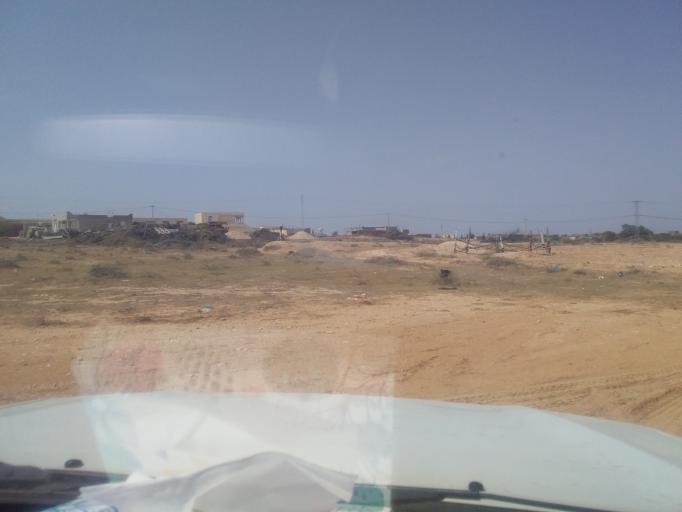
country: TN
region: Madanin
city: Medenine
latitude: 33.5832
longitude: 10.3317
